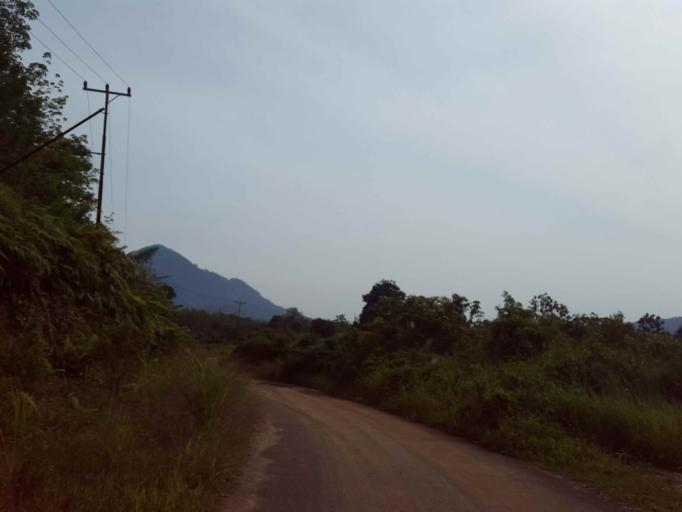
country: MY
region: Sarawak
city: Kuching
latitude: 0.8470
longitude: 110.4436
